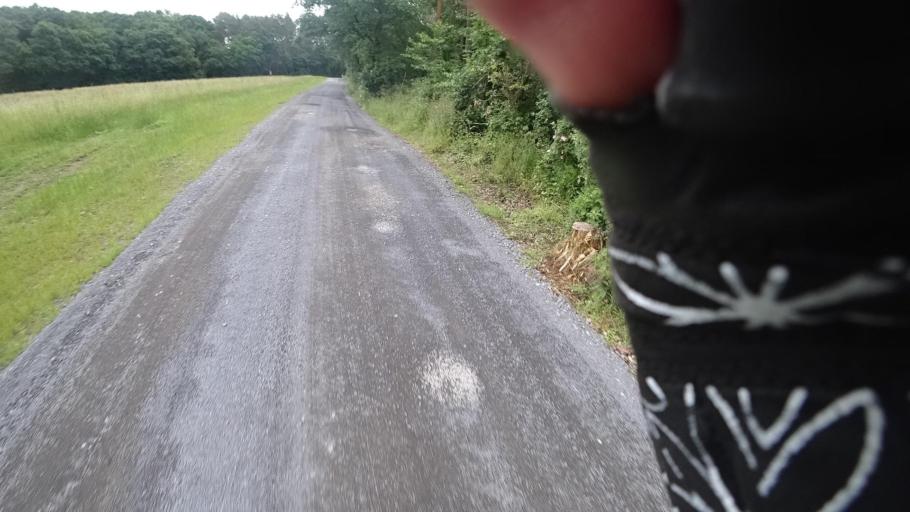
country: DE
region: Rheinland-Pfalz
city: Mayschoss
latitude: 50.5416
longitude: 7.0233
